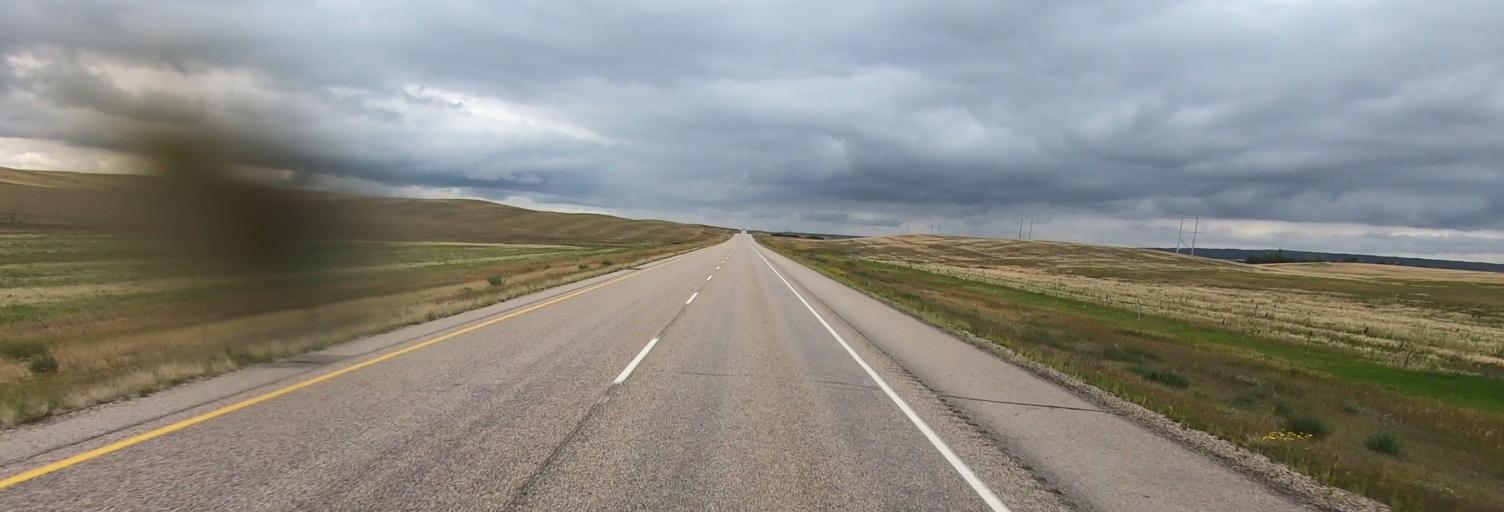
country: CA
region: Saskatchewan
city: Gravelbourg
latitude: 50.4630
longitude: -106.2700
